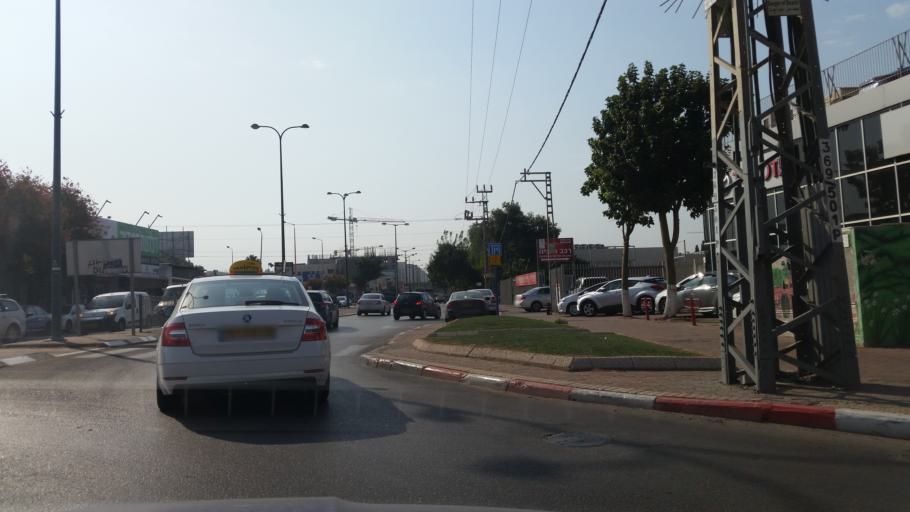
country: IL
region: Central District
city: Bet Yizhaq
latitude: 32.3179
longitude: 34.8739
